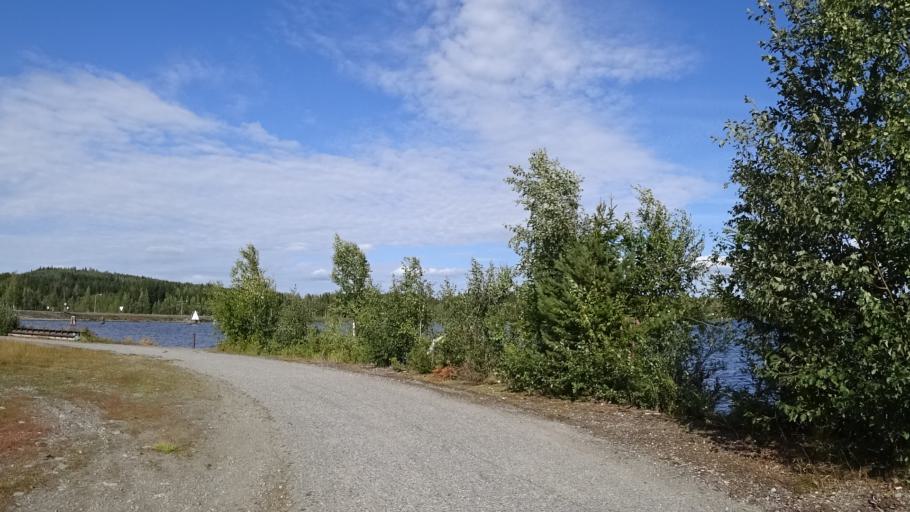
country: FI
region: North Karelia
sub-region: Joensuu
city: Eno
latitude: 62.8007
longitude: 30.1208
